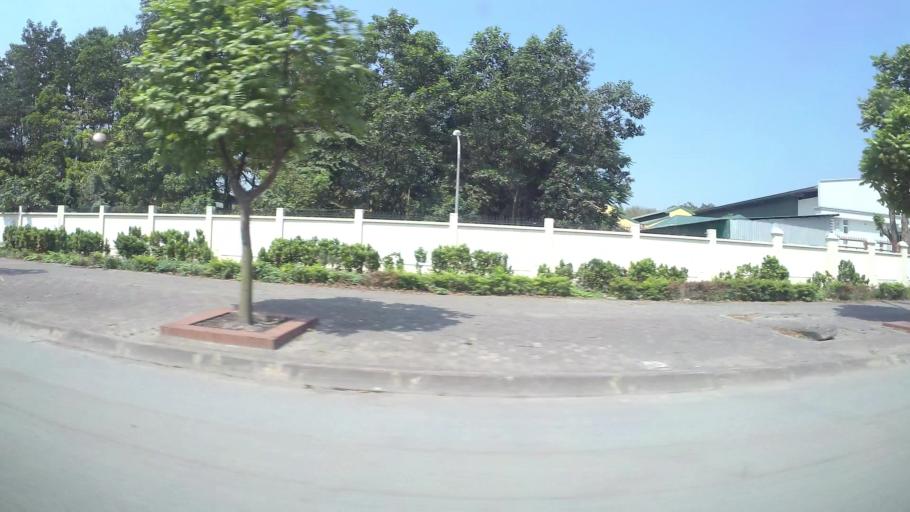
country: VN
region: Ha Noi
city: Hoan Kiem
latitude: 21.0676
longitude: 105.8801
